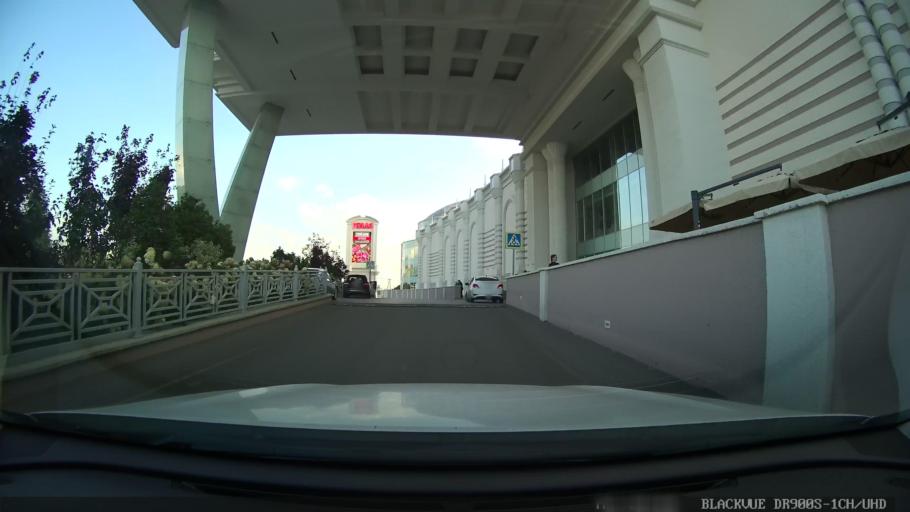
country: RU
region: Moskovskaya
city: Marfino
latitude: 55.7207
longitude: 37.3809
